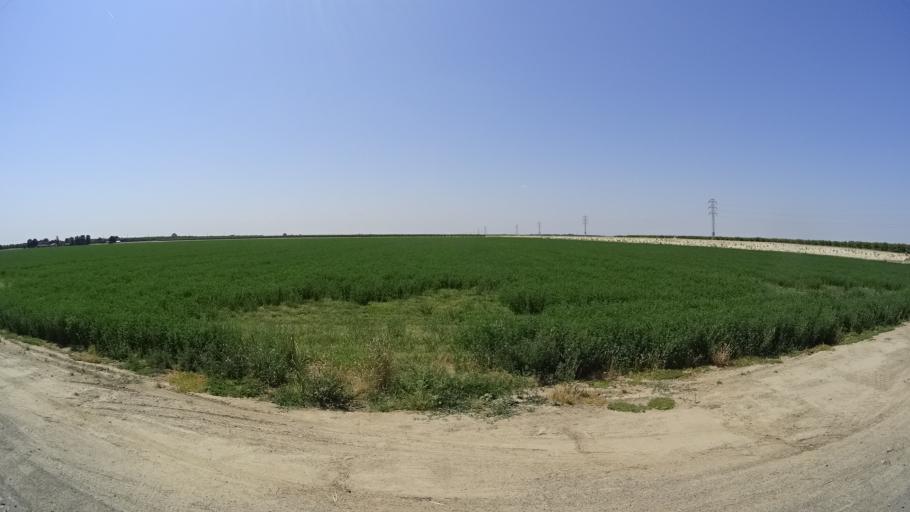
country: US
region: California
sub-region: Kings County
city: Home Garden
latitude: 36.2840
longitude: -119.5906
